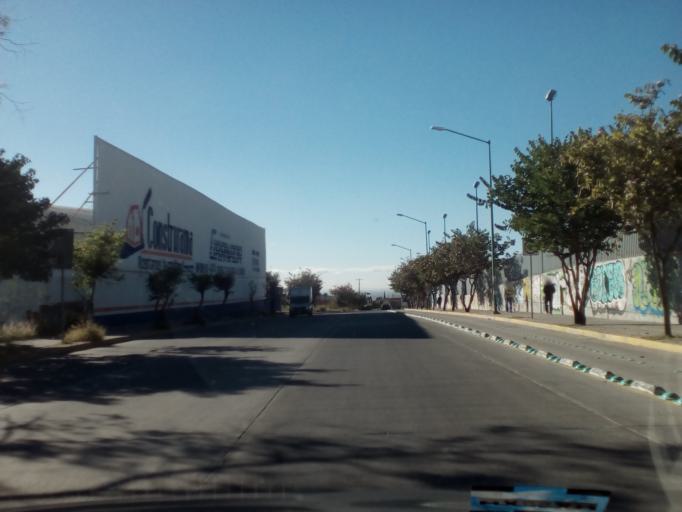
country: MX
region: Guanajuato
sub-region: Leon
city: La Ermita
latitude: 21.1332
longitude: -101.7156
